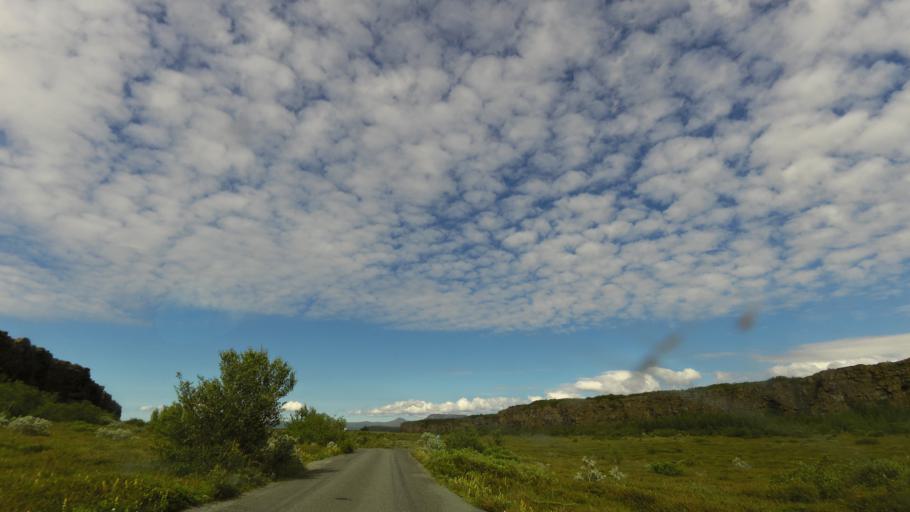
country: IS
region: Northeast
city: Husavik
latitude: 66.0164
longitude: -16.4985
